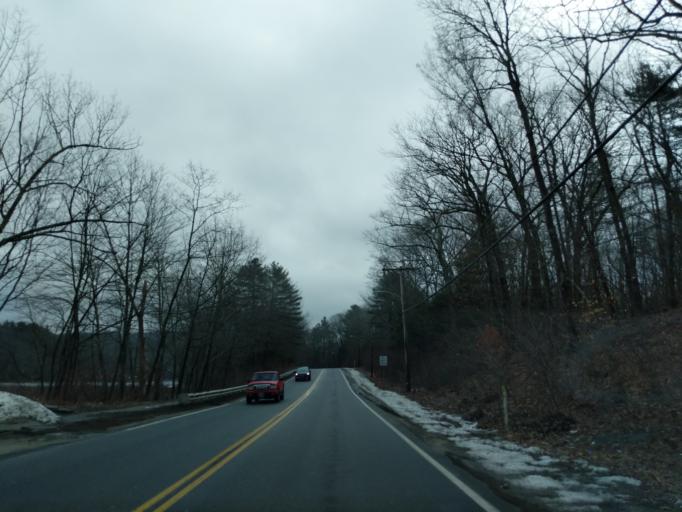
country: US
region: Massachusetts
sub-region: Worcester County
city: Webster
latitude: 42.0606
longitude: -71.8536
